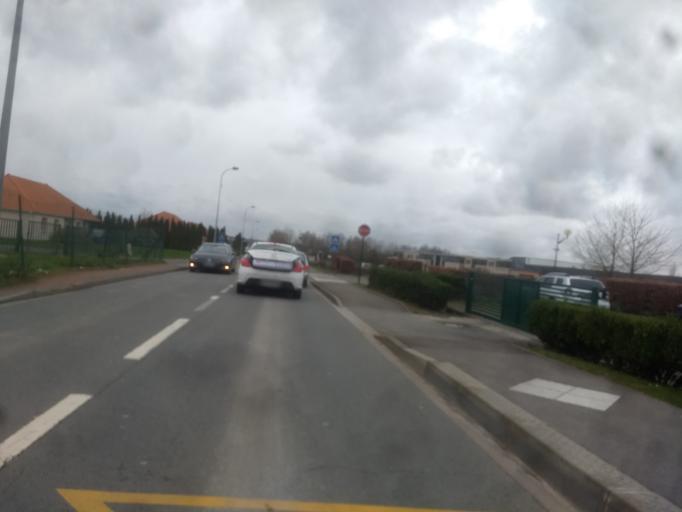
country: FR
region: Nord-Pas-de-Calais
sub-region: Departement du Pas-de-Calais
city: Anzin-Saint-Aubin
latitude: 50.3141
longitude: 2.7566
